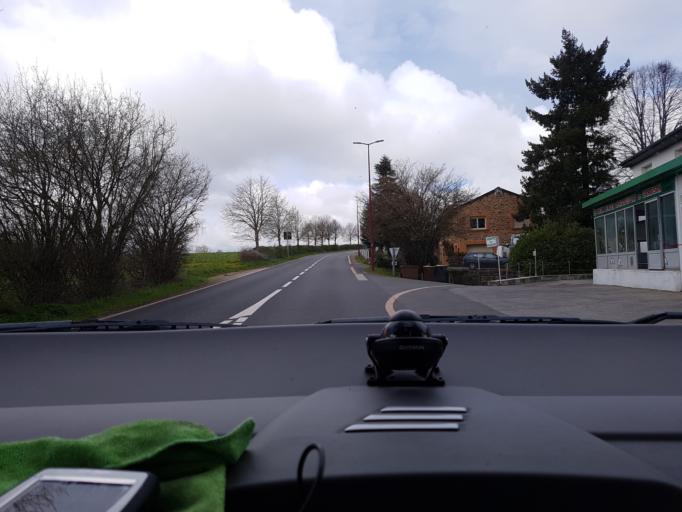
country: FR
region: Midi-Pyrenees
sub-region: Departement de l'Aveyron
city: Colombies
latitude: 44.3943
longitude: 2.3756
